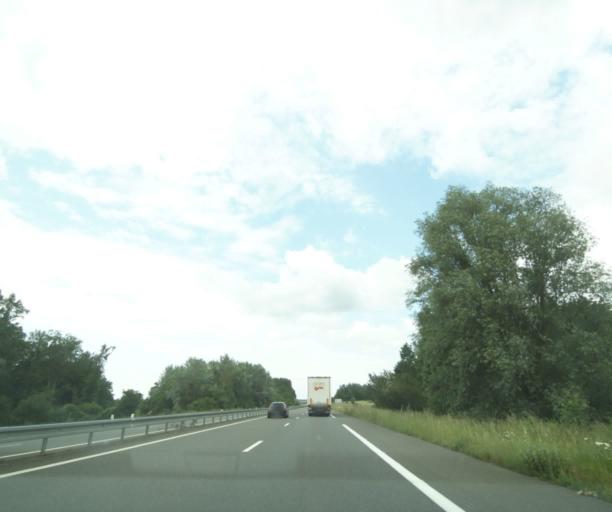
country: FR
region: Pays de la Loire
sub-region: Departement de Maine-et-Loire
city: Vivy
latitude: 47.3201
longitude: -0.0353
